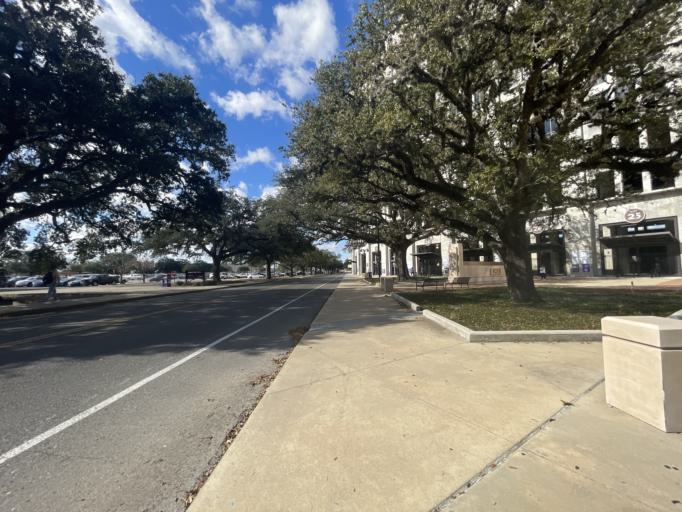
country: US
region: Louisiana
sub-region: East Baton Rouge Parish
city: Baton Rouge
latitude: 30.4106
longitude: -91.1830
